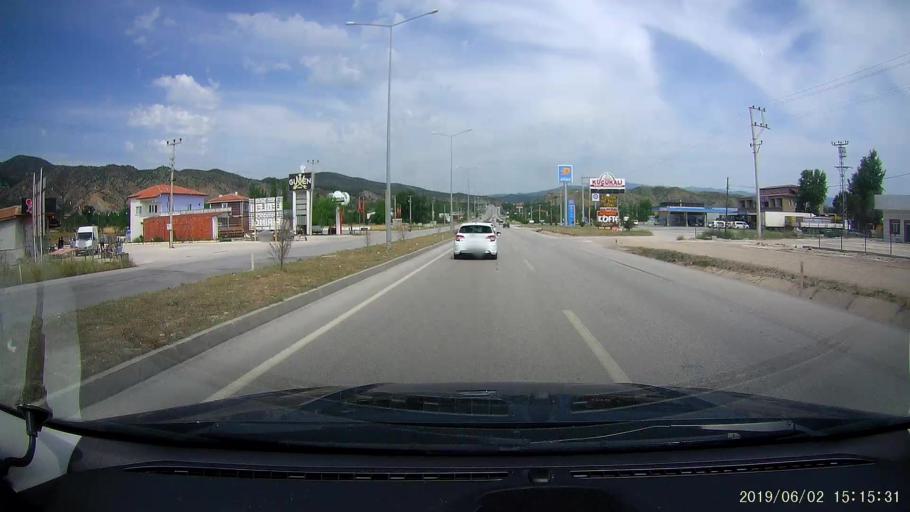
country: TR
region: Corum
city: Osmancik
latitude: 40.9709
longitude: 34.8496
